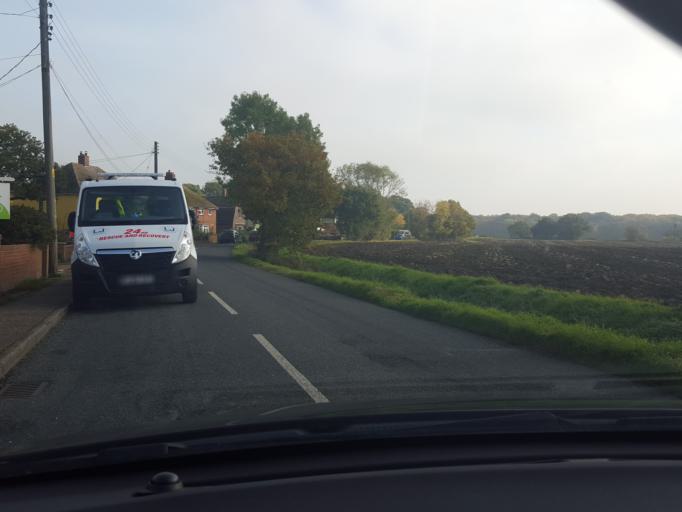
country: GB
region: England
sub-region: Essex
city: Mistley
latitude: 51.9378
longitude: 1.1717
